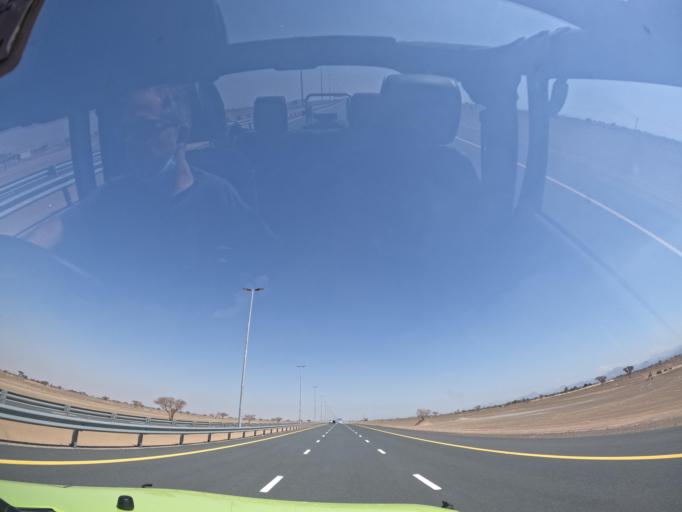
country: AE
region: Ash Shariqah
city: Adh Dhayd
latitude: 25.0885
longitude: 55.9200
